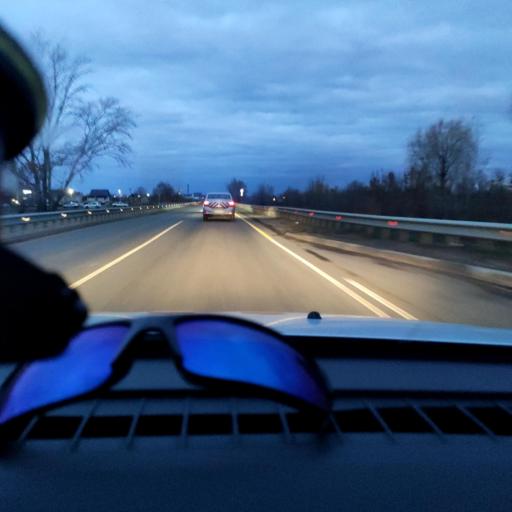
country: RU
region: Samara
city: Samara
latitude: 53.1175
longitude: 50.1227
